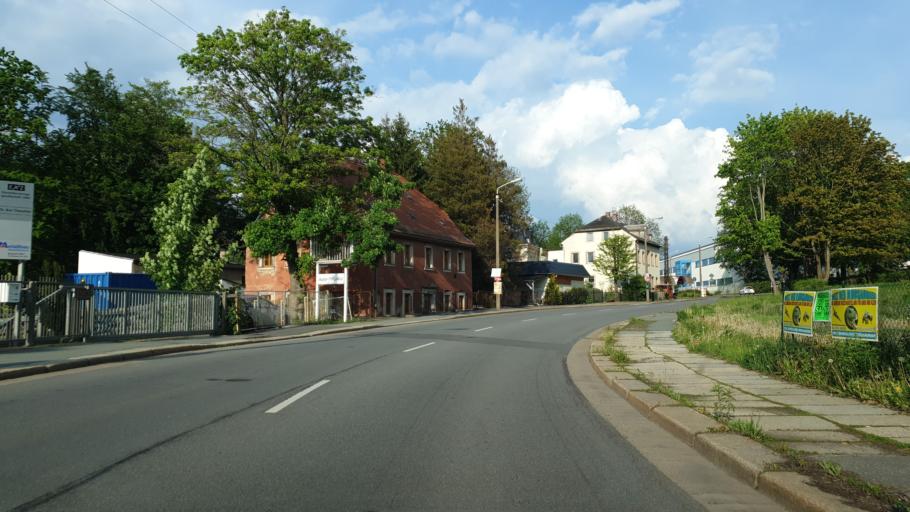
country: DE
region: Saxony
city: Neukirchen
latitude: 50.8194
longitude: 12.8729
